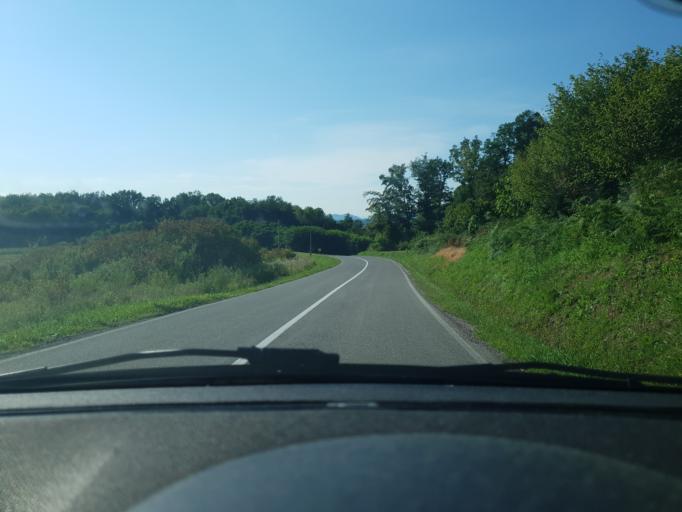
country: HR
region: Zagrebacka
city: Jakovlje
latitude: 45.9154
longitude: 15.8434
